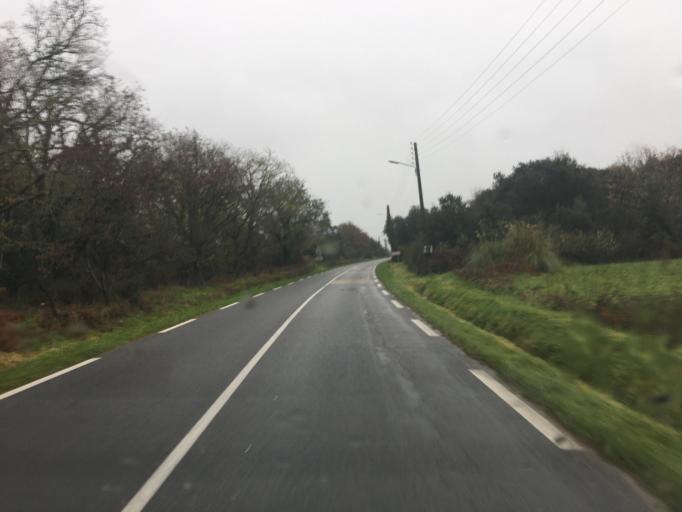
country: FR
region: Pays de la Loire
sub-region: Departement de la Loire-Atlantique
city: La Turballe
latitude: 47.3399
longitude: -2.4721
